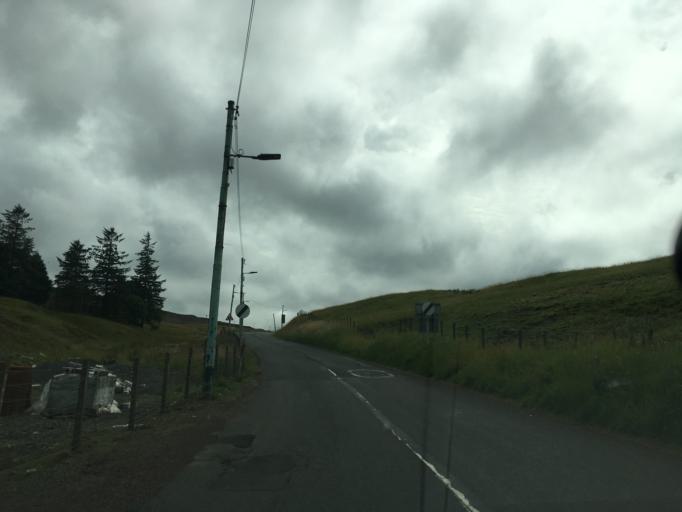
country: GB
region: Scotland
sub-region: South Lanarkshire
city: Douglas
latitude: 55.4121
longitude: -3.7637
